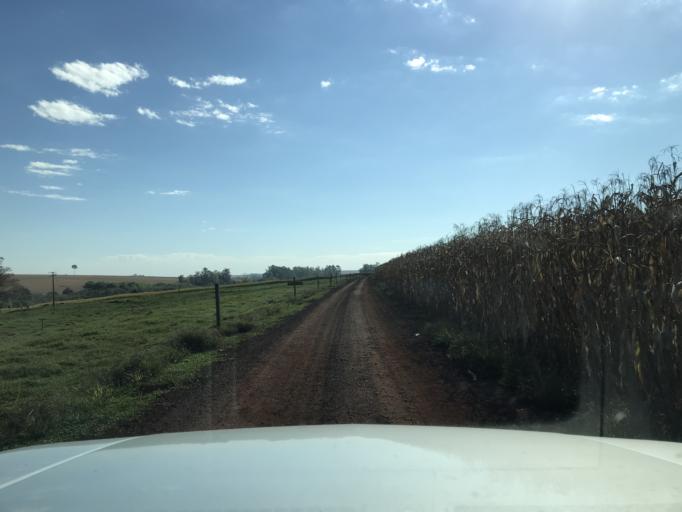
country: BR
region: Parana
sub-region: Palotina
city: Palotina
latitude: -24.2665
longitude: -53.8147
